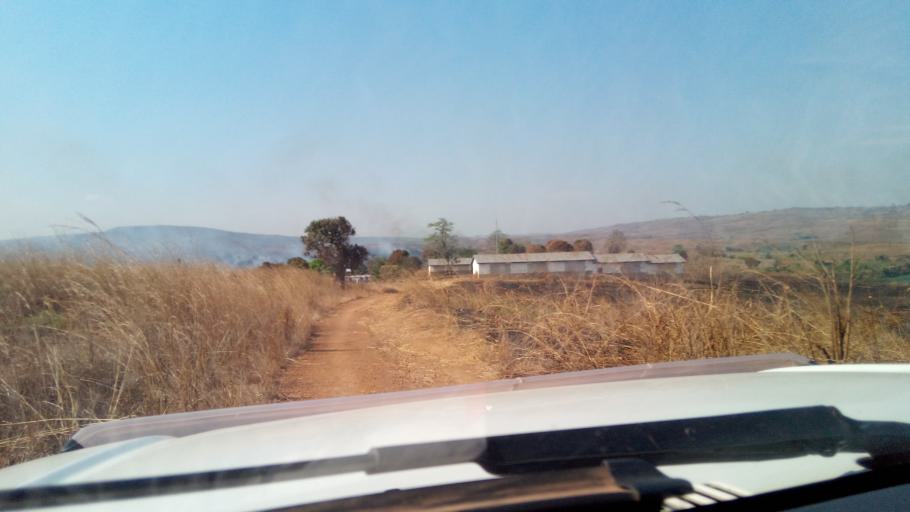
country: CD
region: Katanga
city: Kalemie
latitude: -5.9048
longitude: 29.1258
